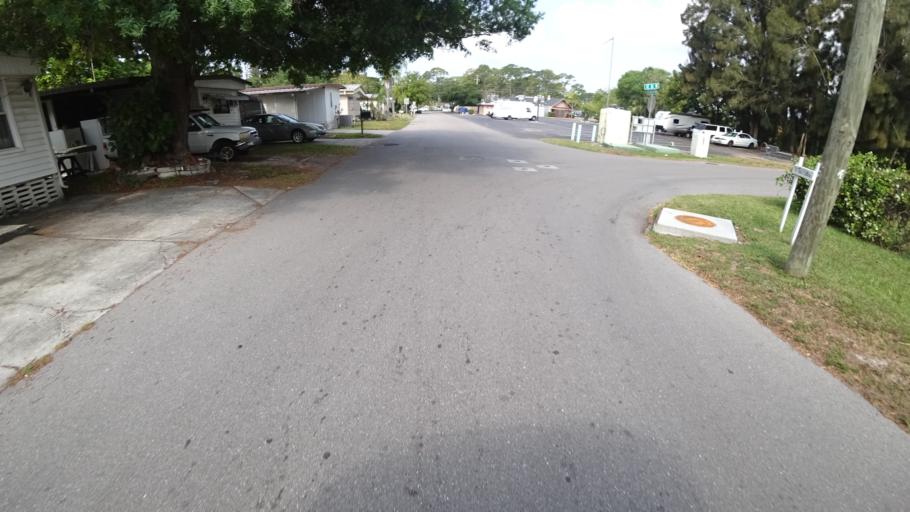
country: US
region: Florida
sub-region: Manatee County
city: South Bradenton
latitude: 27.4513
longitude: -82.5737
